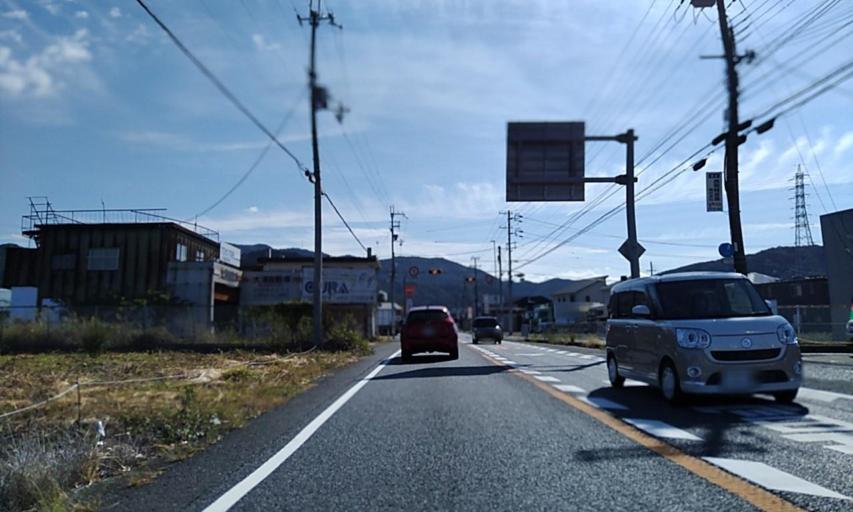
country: JP
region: Wakayama
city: Kainan
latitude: 34.0205
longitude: 135.1801
